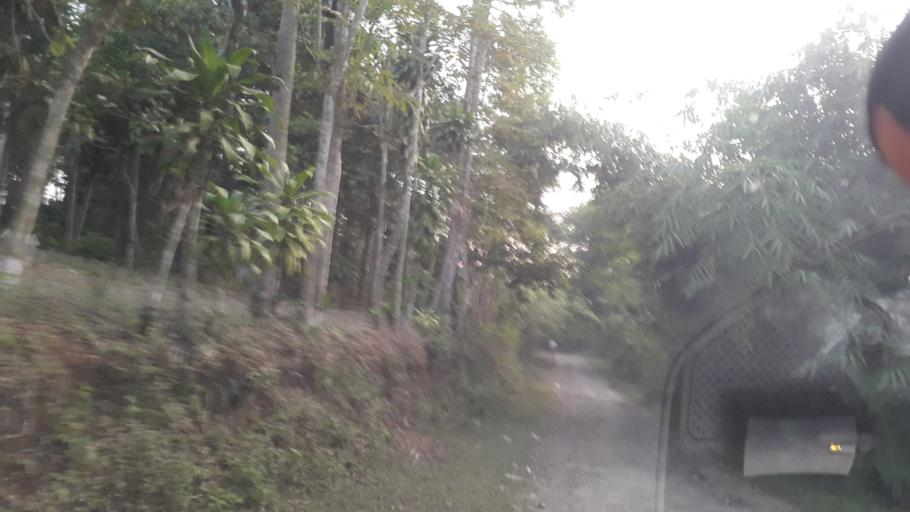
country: ID
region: West Java
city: Cicurug
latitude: -6.8466
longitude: 106.8322
